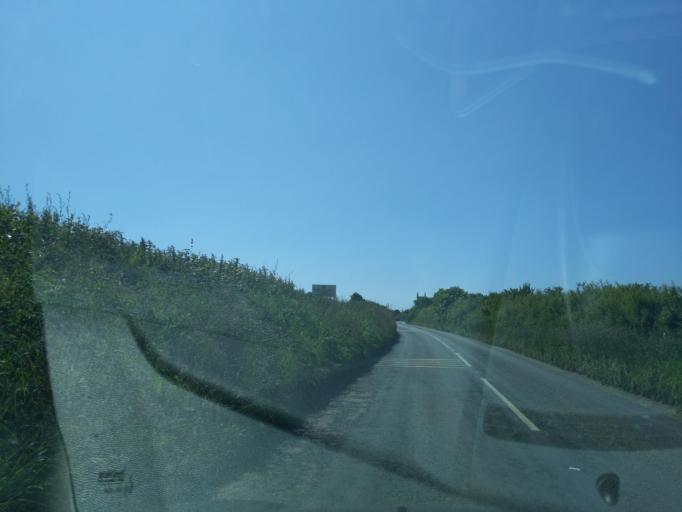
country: GB
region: England
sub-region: Cornwall
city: Wadebridge
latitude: 50.5734
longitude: -4.8250
